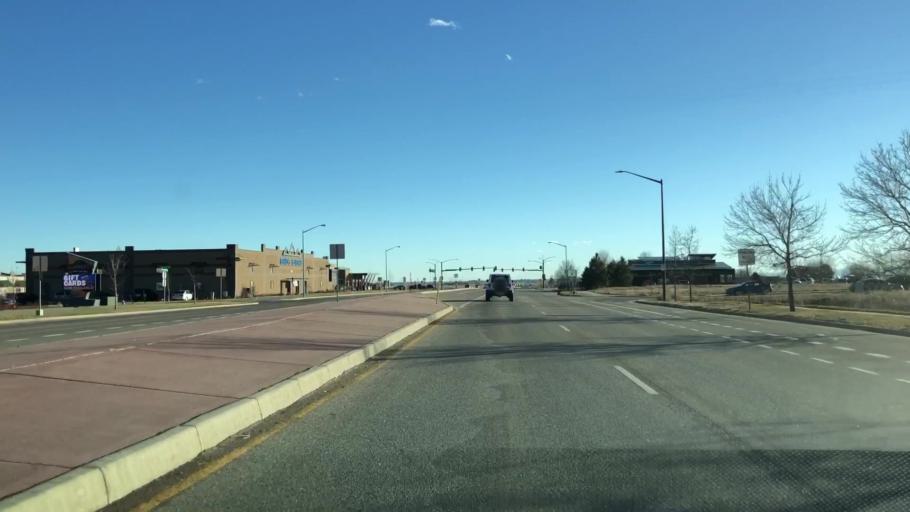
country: US
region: Colorado
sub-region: Weld County
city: Windsor
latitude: 40.4384
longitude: -104.9826
